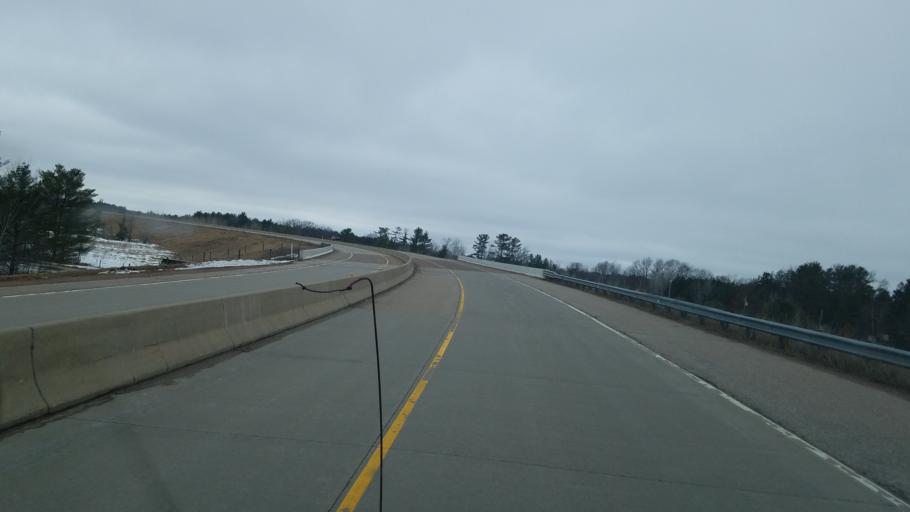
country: US
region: Wisconsin
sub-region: Portage County
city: Stevens Point
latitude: 44.5973
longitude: -89.6076
